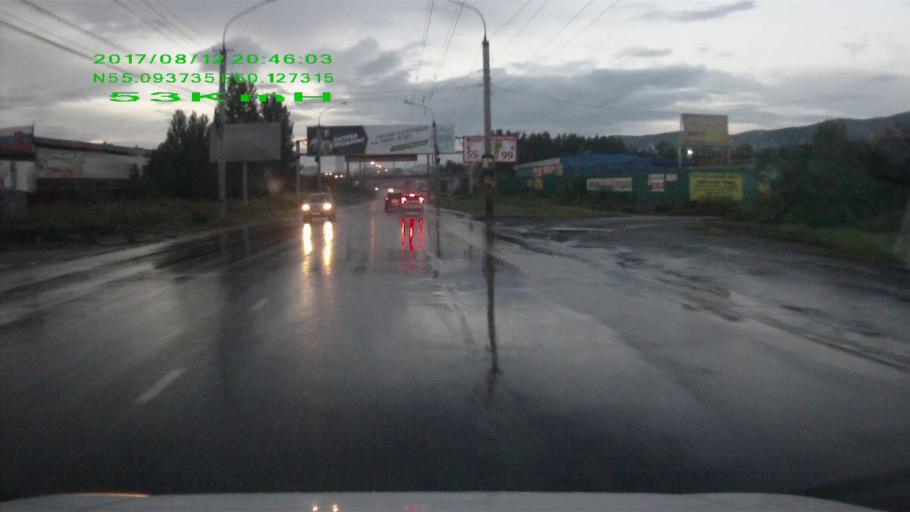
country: RU
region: Chelyabinsk
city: Miass
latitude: 55.0940
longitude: 60.1275
